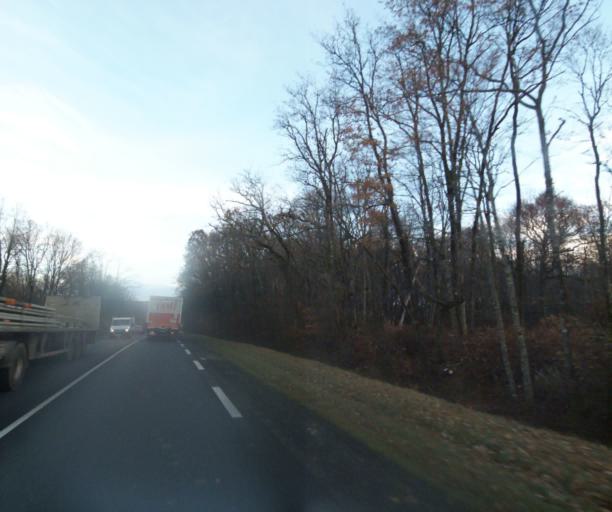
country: FR
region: Poitou-Charentes
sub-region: Departement de la Charente-Maritime
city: Fontcouverte
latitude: 45.7923
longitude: -0.5683
